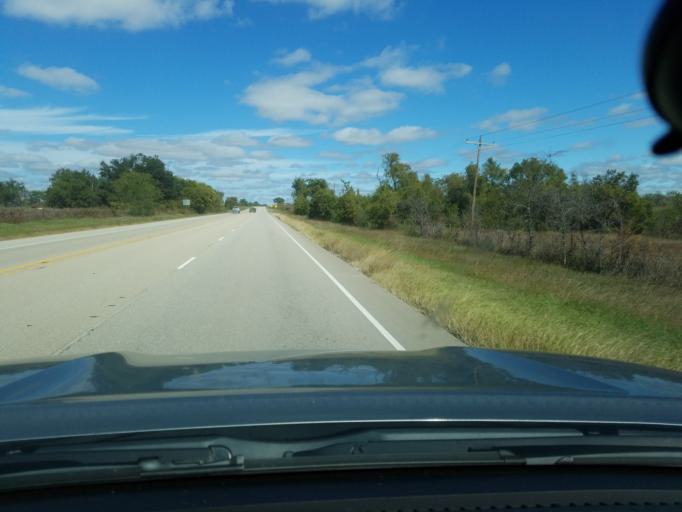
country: US
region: Texas
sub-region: Hamilton County
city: Hamilton
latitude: 31.6528
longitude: -98.1452
